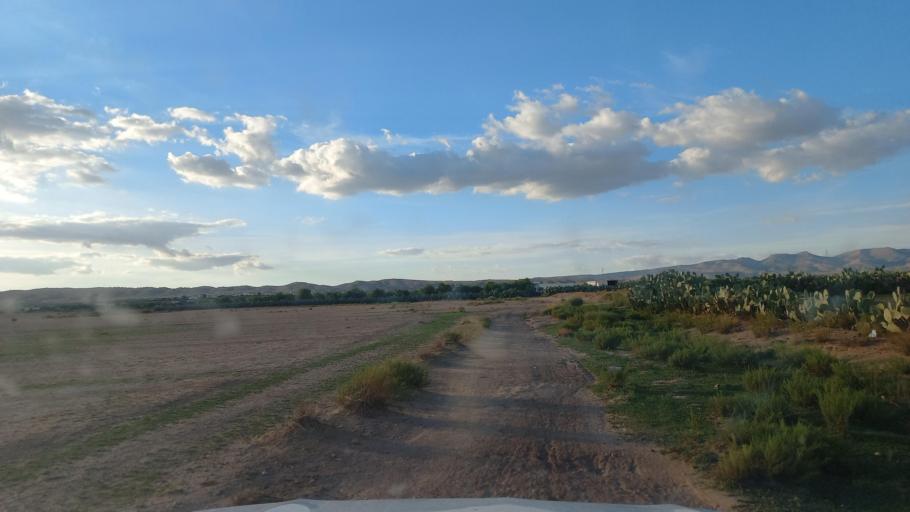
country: TN
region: Al Qasrayn
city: Sbiba
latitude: 35.3537
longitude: 9.0317
